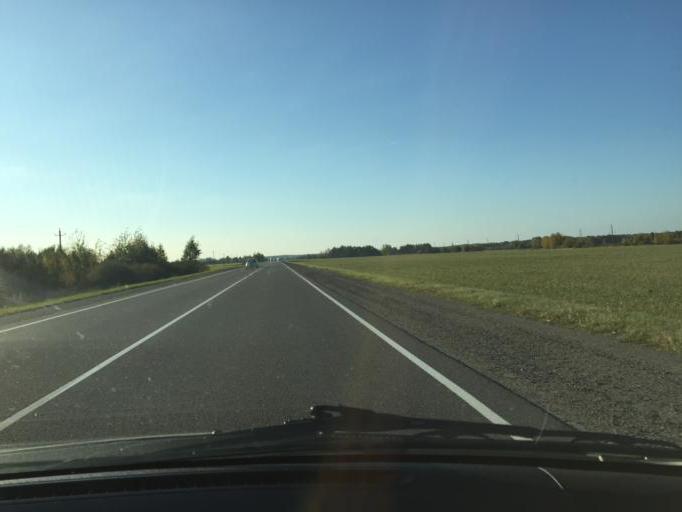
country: BY
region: Brest
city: Horad Luninyets
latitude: 52.3137
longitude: 26.6519
